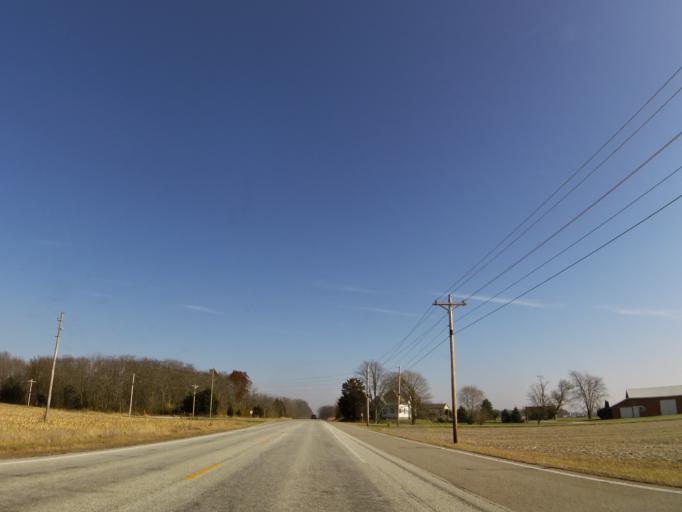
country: US
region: Indiana
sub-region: Shelby County
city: Shelbyville
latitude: 39.5436
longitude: -85.6957
